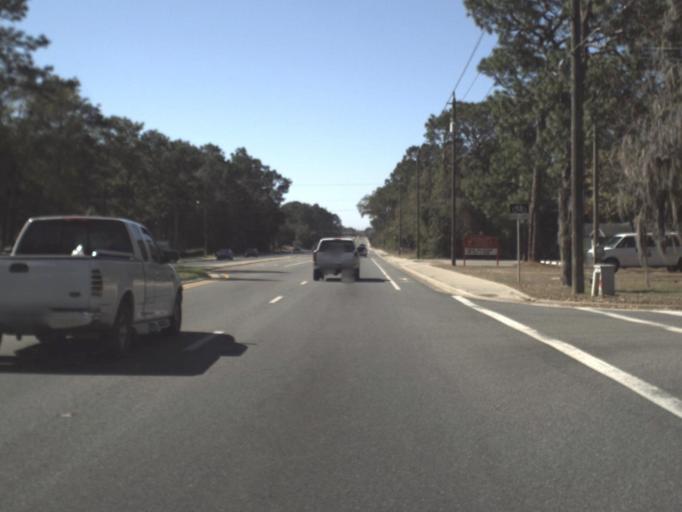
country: US
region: Florida
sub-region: Leon County
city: Tallahassee
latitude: 30.3886
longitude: -84.2863
